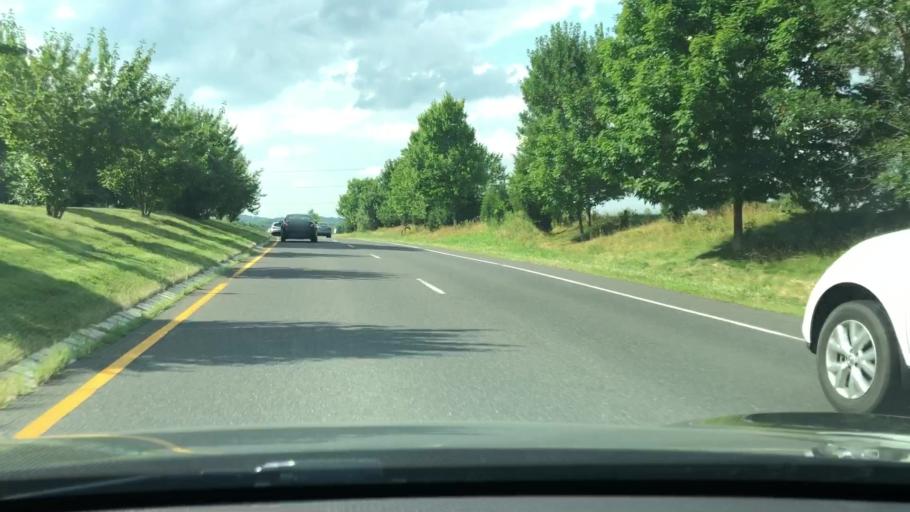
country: US
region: New Jersey
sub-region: Mercer County
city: Pennington
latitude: 40.3044
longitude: -74.8119
